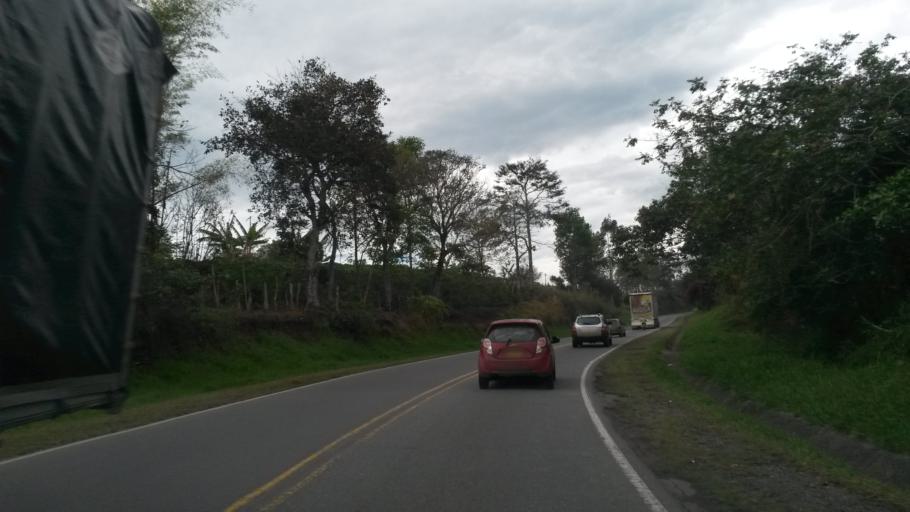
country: CO
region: Cauca
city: Rosas
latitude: 2.3421
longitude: -76.6923
